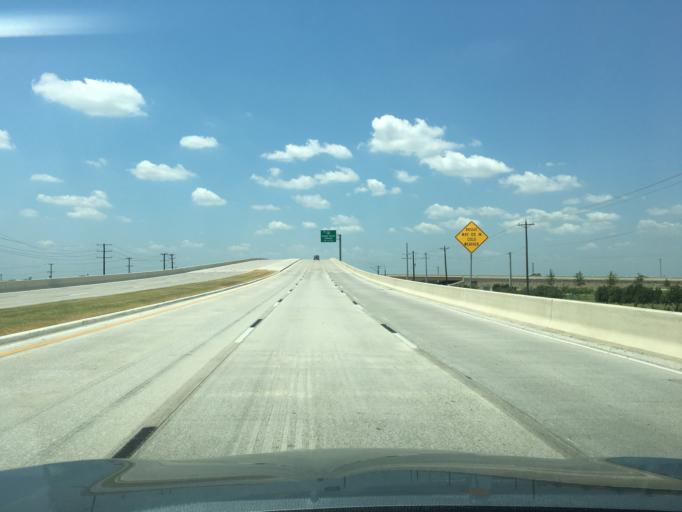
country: US
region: Texas
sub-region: Collin County
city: Prosper
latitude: 33.2189
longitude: -96.7987
